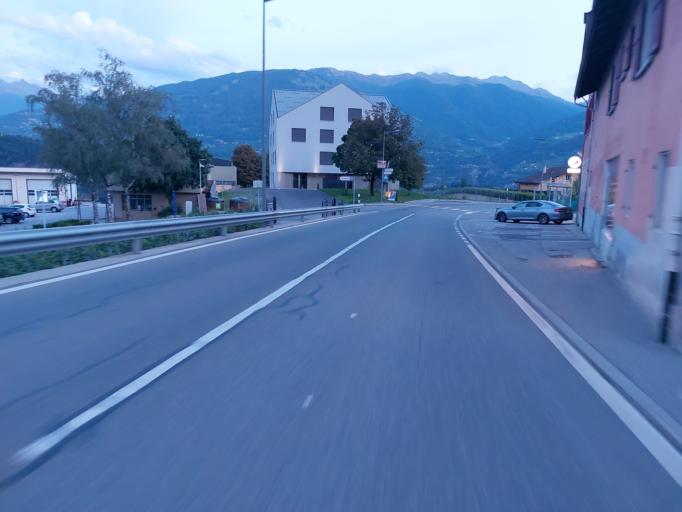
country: CH
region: Valais
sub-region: Conthey District
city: Conthey
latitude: 46.2353
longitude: 7.3048
